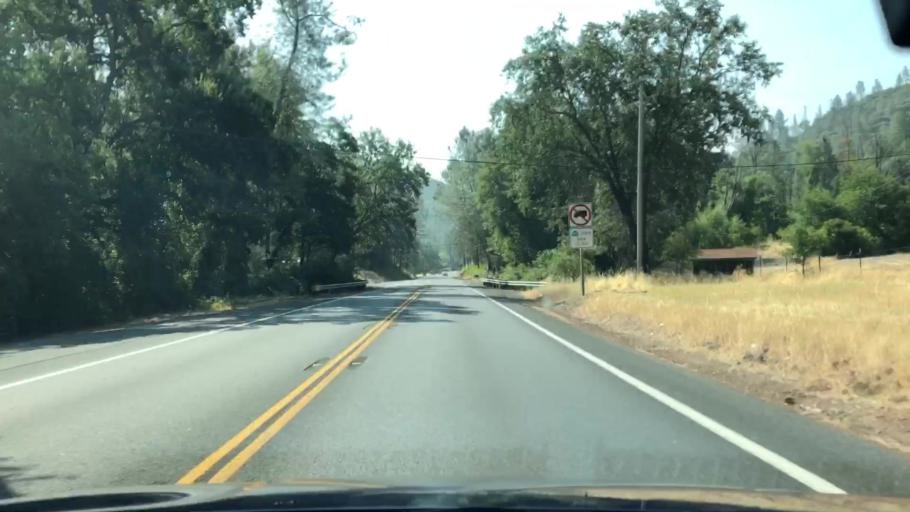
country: US
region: California
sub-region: Lake County
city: Middletown
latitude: 38.7004
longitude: -122.6023
